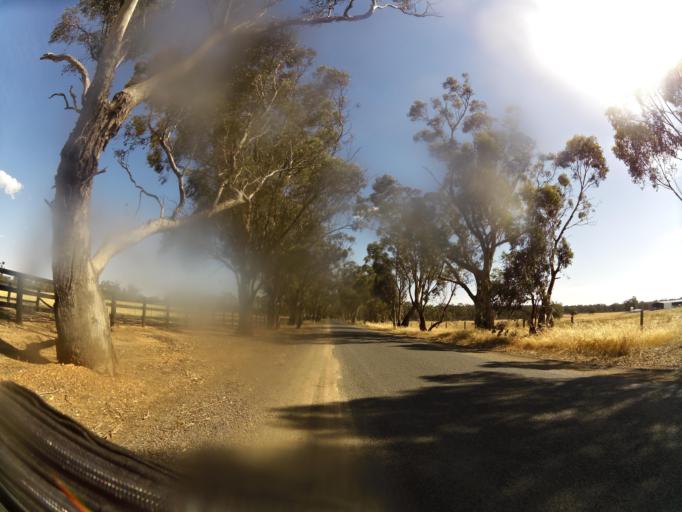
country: AU
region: Victoria
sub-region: Campaspe
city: Kyabram
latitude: -36.8633
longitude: 145.0878
